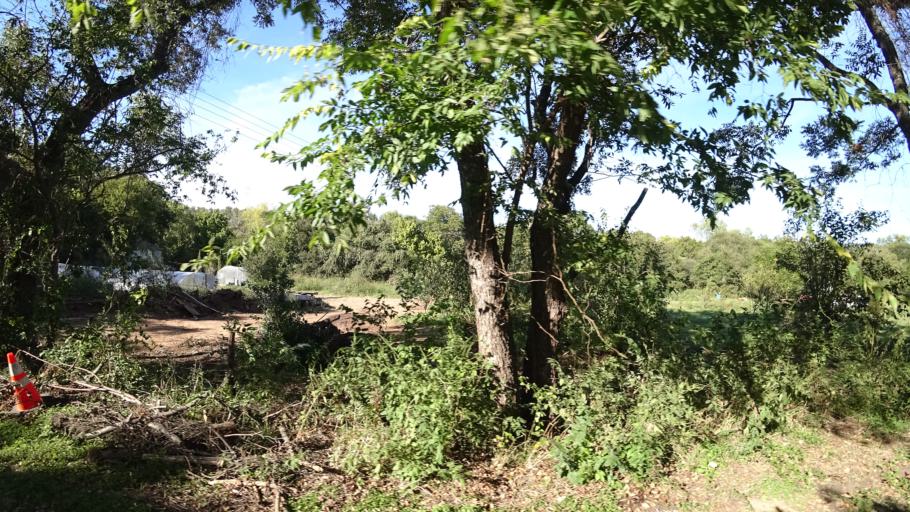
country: US
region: Texas
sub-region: Travis County
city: Austin
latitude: 30.2618
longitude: -97.6672
